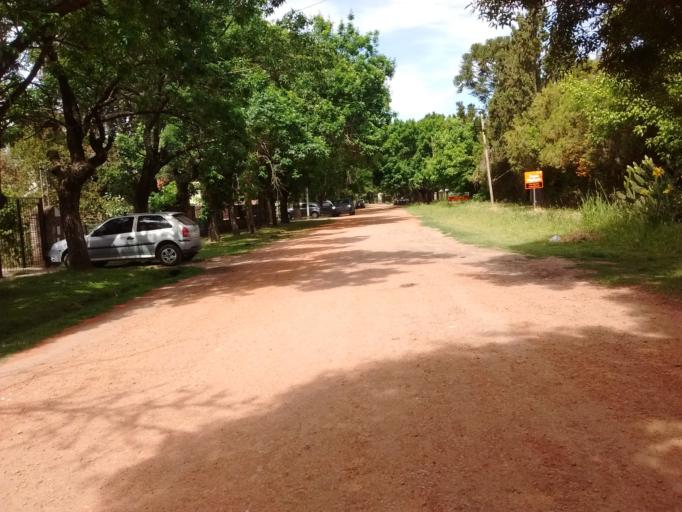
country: AR
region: Santa Fe
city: Funes
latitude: -32.9113
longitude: -60.8042
